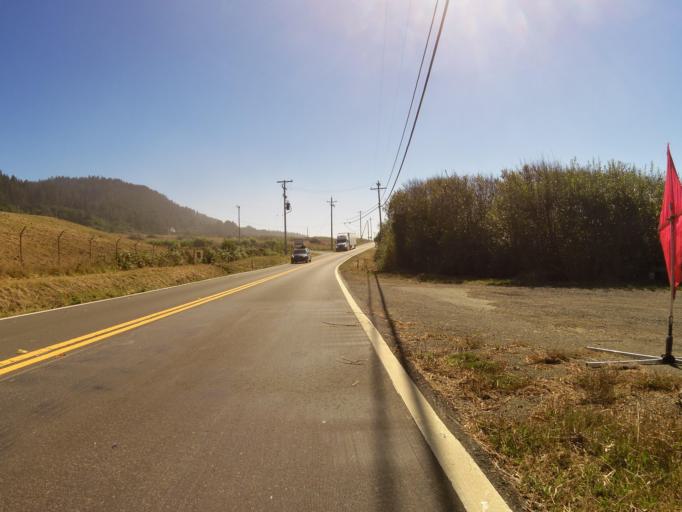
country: US
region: California
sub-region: Mendocino County
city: Fort Bragg
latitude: 39.6428
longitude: -123.7843
